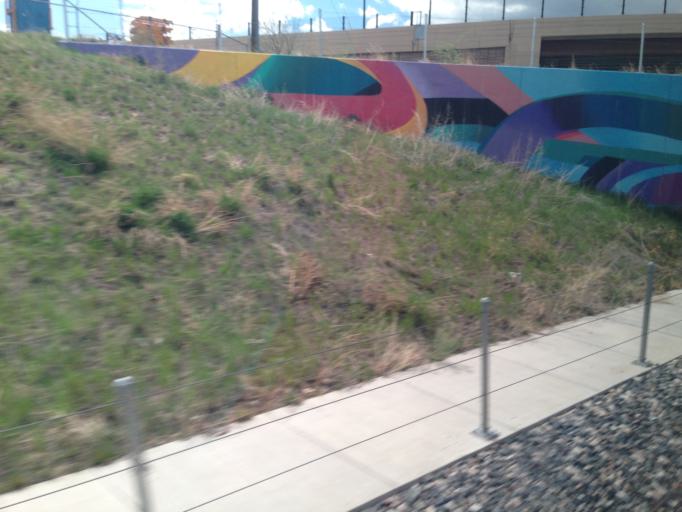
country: US
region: Colorado
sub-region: Adams County
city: Twin Lakes
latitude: 39.8049
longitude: -105.0049
